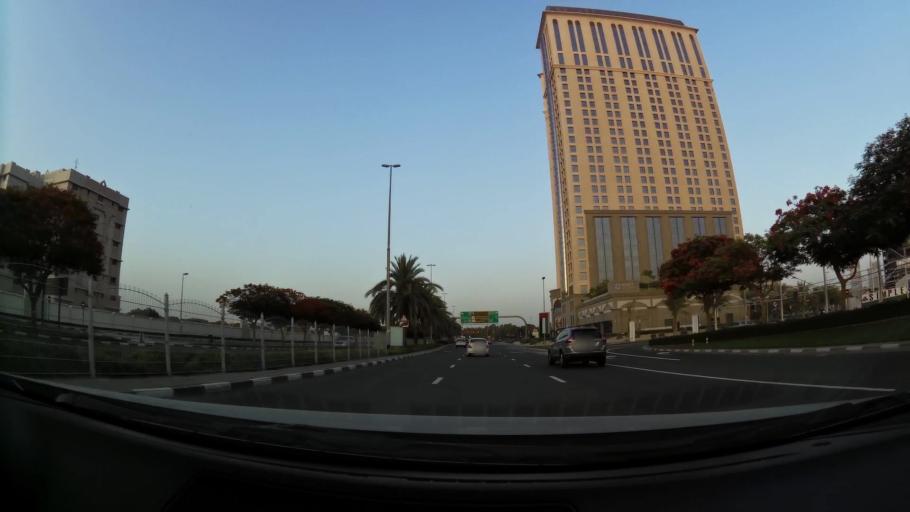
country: AE
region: Ash Shariqah
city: Sharjah
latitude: 25.2349
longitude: 55.3220
